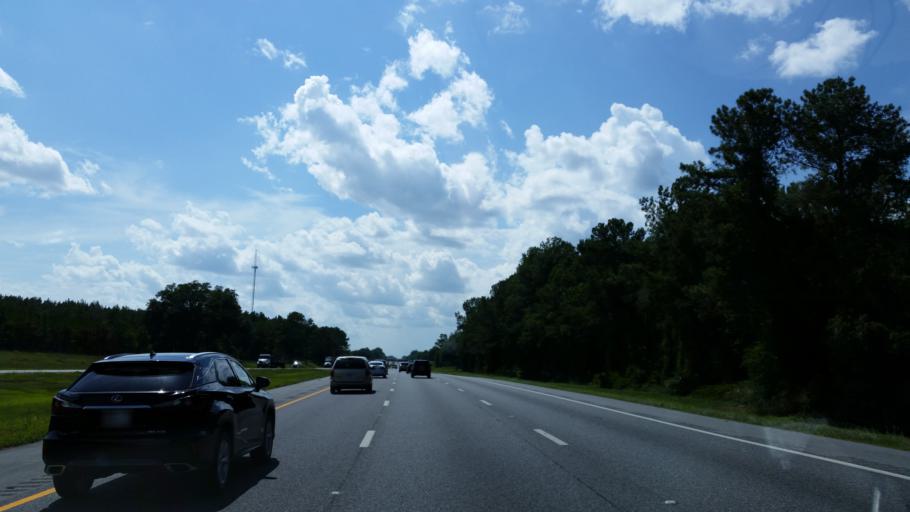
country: US
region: Florida
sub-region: Hamilton County
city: Jasper
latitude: 30.4803
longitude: -82.9856
